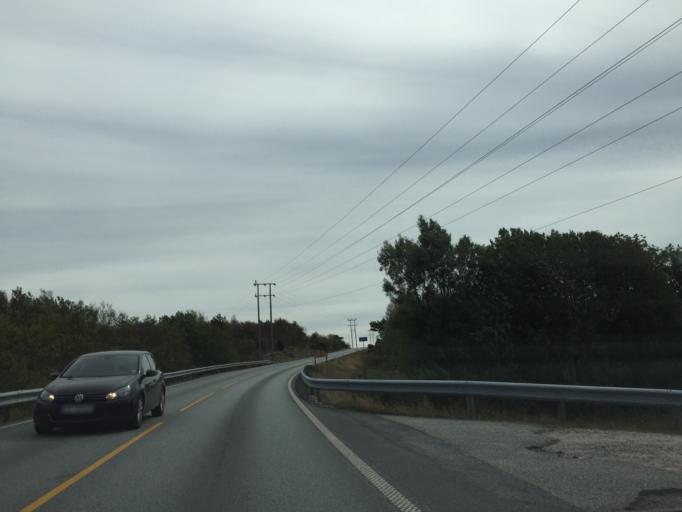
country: NO
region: Ostfold
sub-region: Hvaler
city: Skjaerhalden
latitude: 59.0537
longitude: 10.9482
